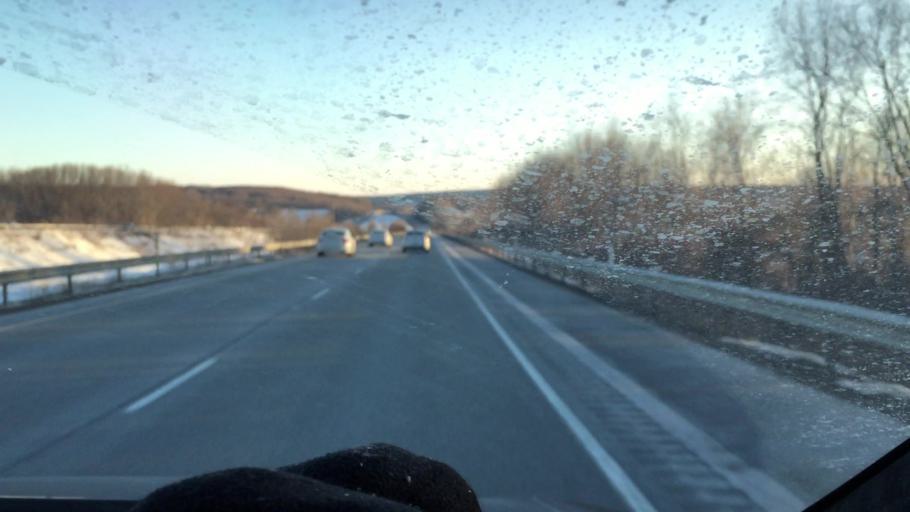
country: US
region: Pennsylvania
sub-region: Crawford County
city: Meadville
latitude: 41.6981
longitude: -80.2013
